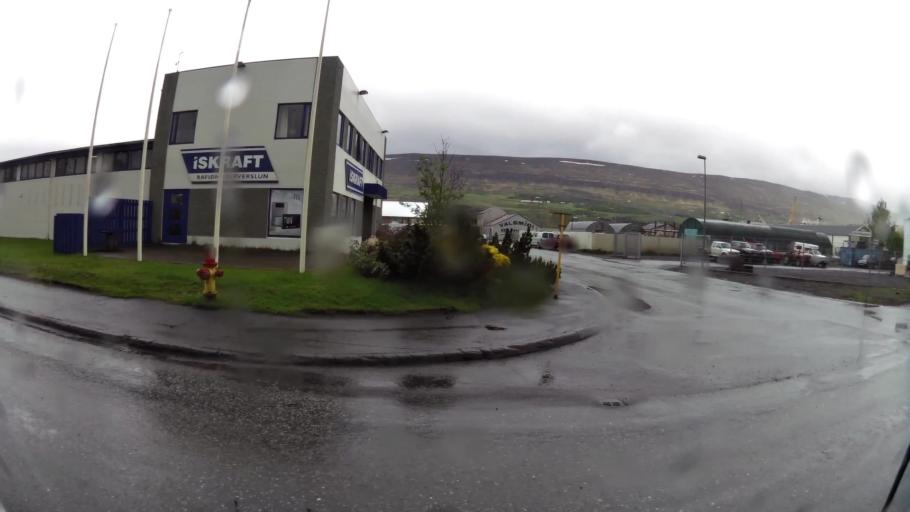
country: IS
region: Northeast
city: Akureyri
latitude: 65.6862
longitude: -18.0833
